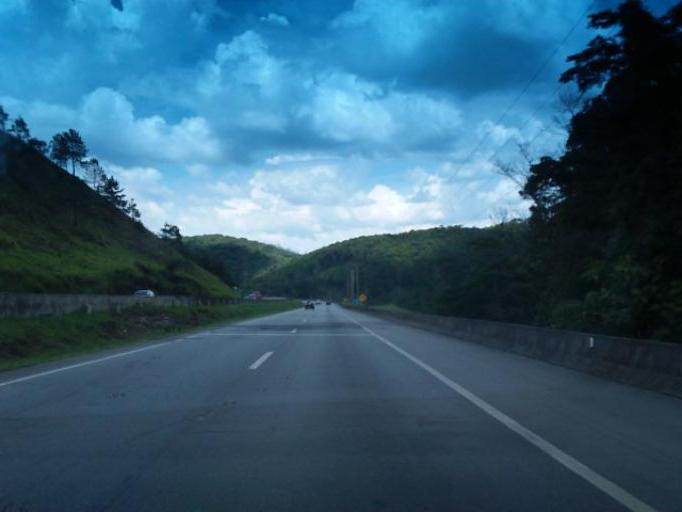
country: BR
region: Sao Paulo
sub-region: Juquitiba
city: Juquitiba
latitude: -24.0026
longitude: -47.1538
